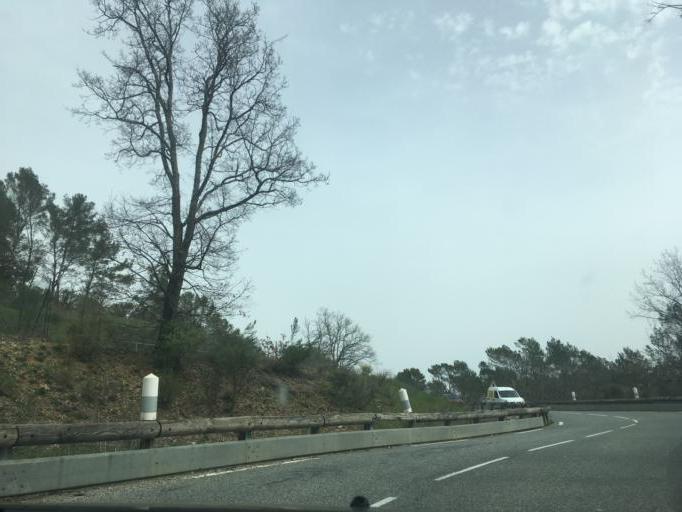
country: FR
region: Provence-Alpes-Cote d'Azur
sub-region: Departement du Var
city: Callian
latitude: 43.5892
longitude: 6.7303
